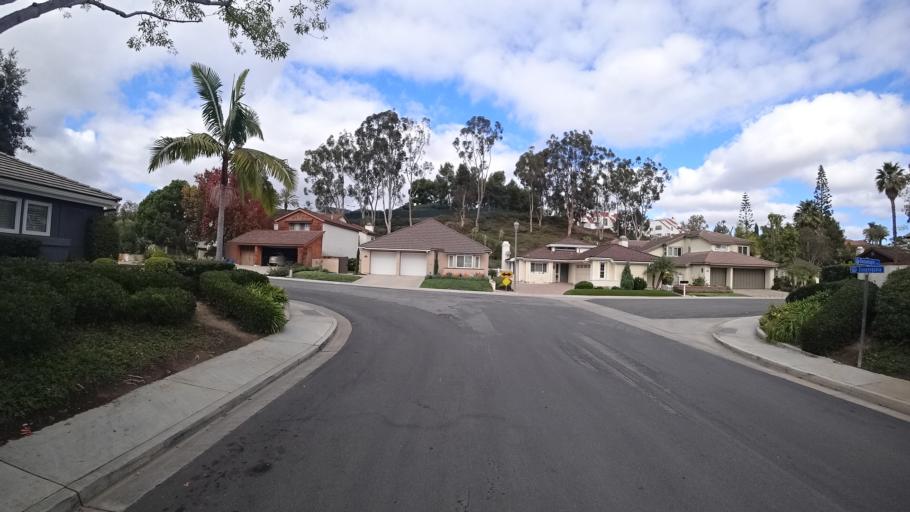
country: US
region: California
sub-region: Orange County
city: Dana Point
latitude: 33.4870
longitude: -117.6949
